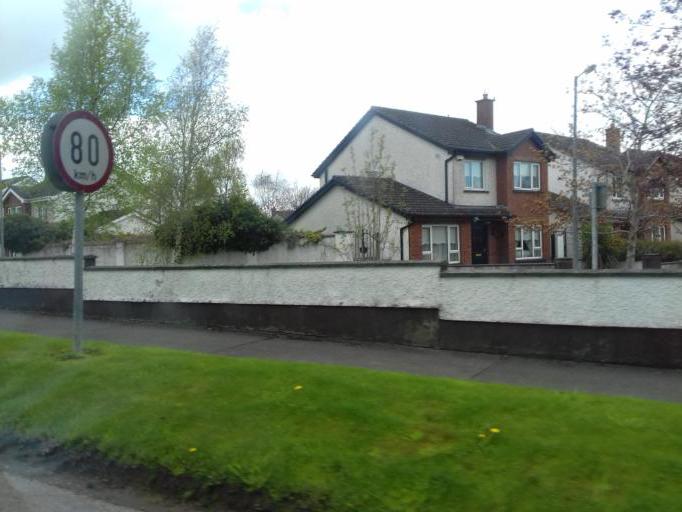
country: IE
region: Leinster
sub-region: Kildare
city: Kildare
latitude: 53.1601
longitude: -6.9166
